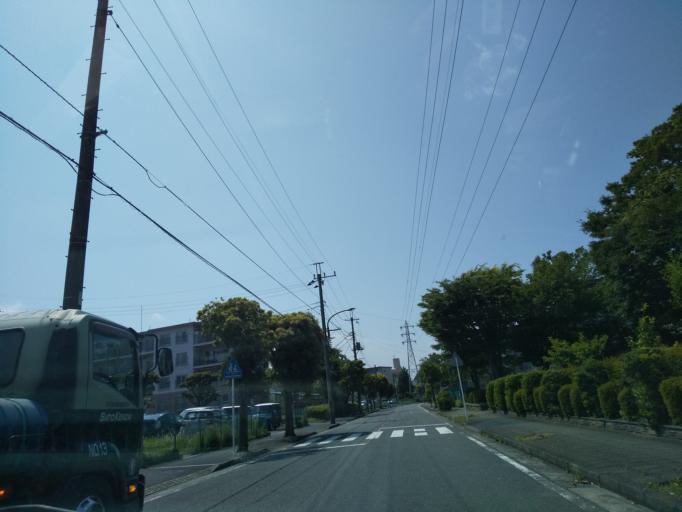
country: JP
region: Kanagawa
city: Zama
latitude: 35.5134
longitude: 139.4099
